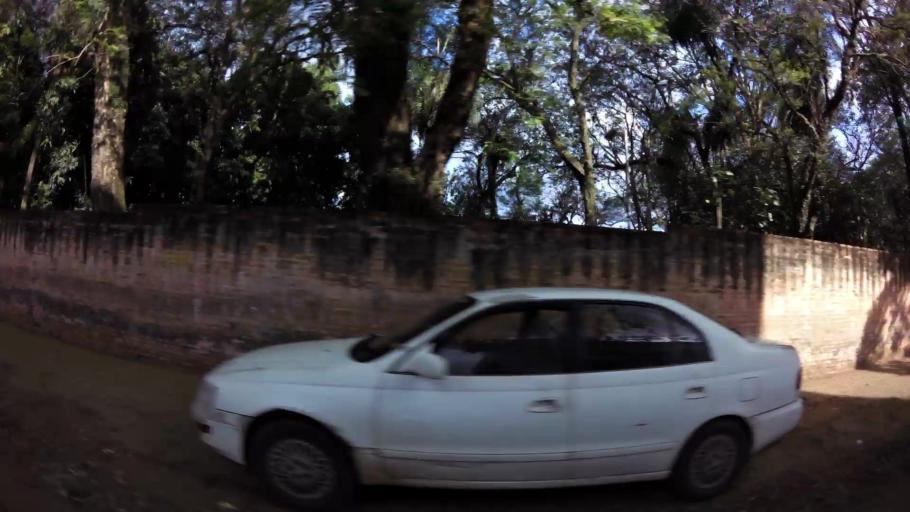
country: PY
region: Central
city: Villa Elisa
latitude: -25.3393
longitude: -57.5640
